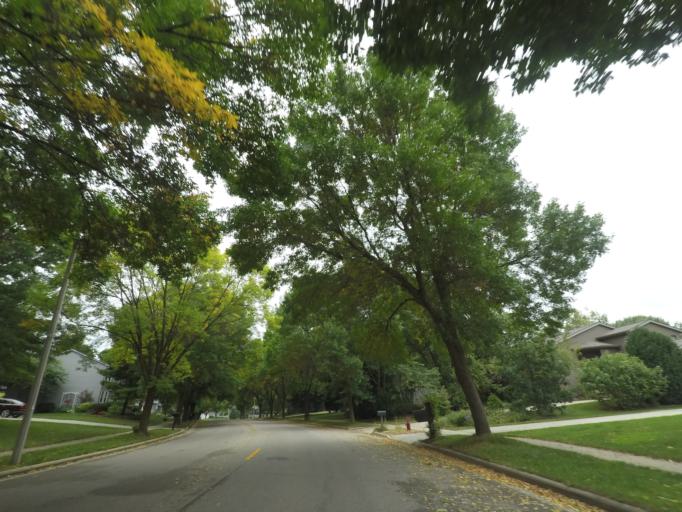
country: US
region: Wisconsin
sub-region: Dane County
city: Middleton
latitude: 43.0848
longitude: -89.5116
